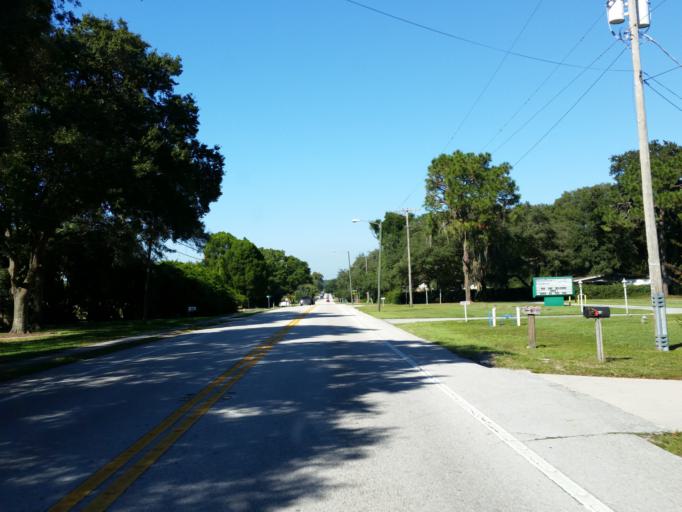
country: US
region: Florida
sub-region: Hillsborough County
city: Bloomingdale
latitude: 27.9109
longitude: -82.2590
